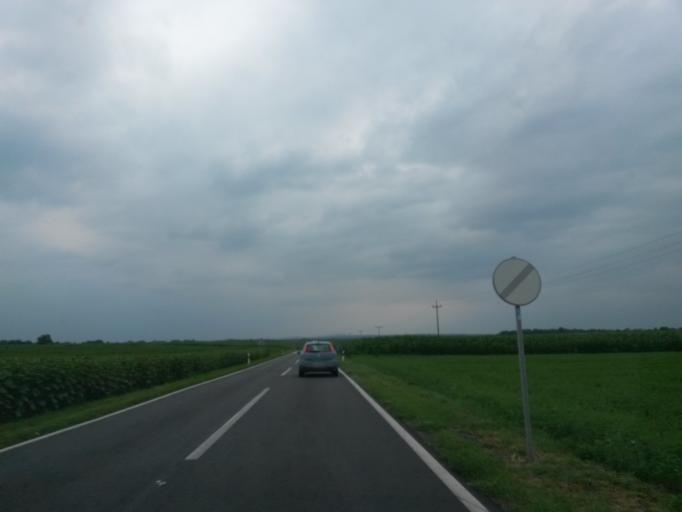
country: HR
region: Vukovarsko-Srijemska
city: Bapska
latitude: 45.2458
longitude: 19.2267
